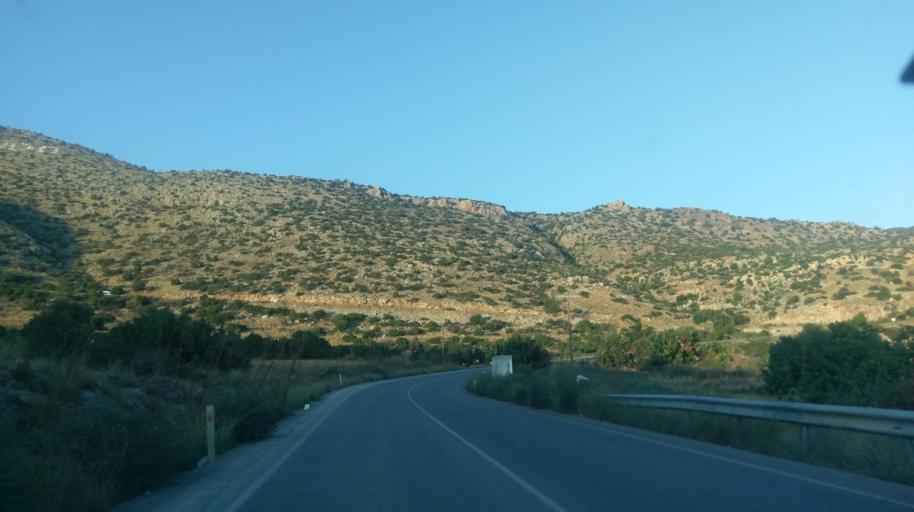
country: CY
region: Lefkosia
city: Nicosia
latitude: 35.2714
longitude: 33.4870
